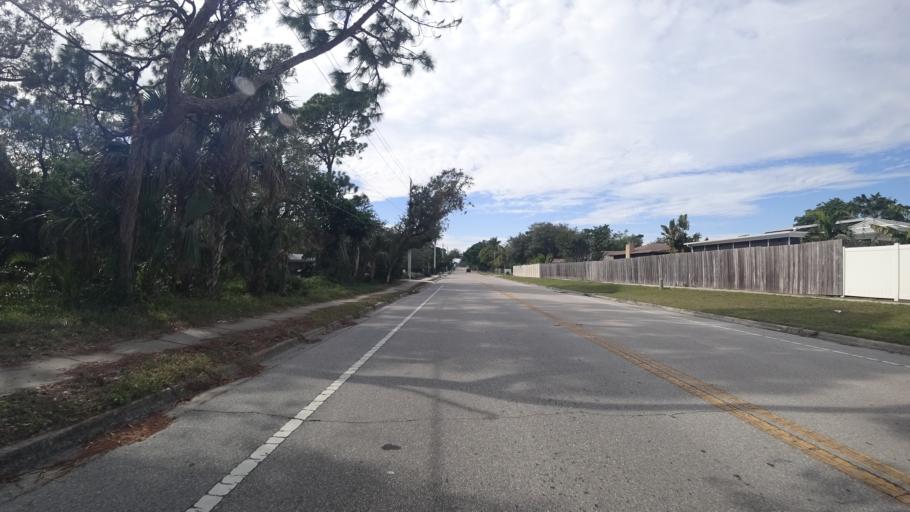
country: US
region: Florida
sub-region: Manatee County
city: West Bradenton
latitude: 27.5071
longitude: -82.6392
